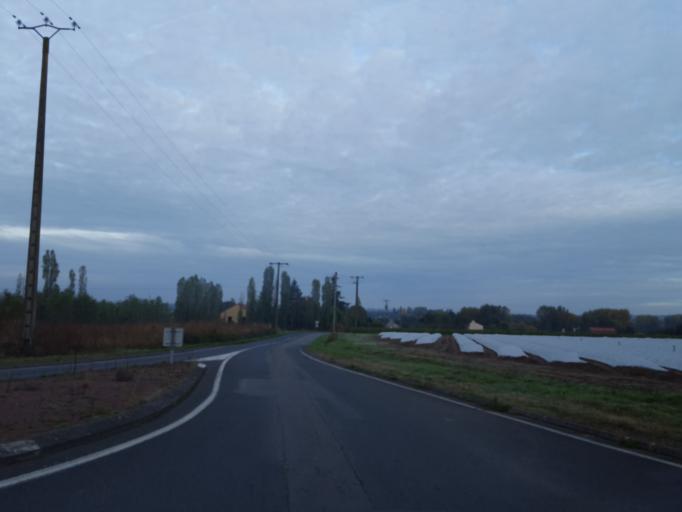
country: FR
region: Pays de la Loire
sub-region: Departement de la Loire-Atlantique
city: Saint-Julien-de-Concelles
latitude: 47.2472
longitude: -1.4007
